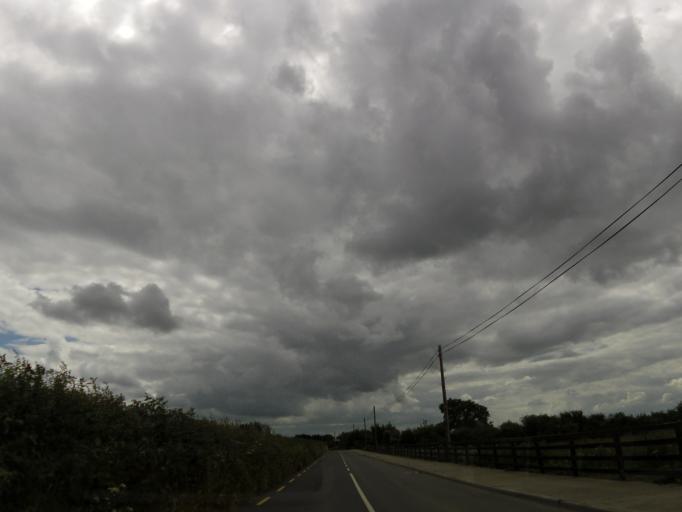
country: IE
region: Munster
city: Thurles
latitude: 52.6760
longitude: -7.7993
